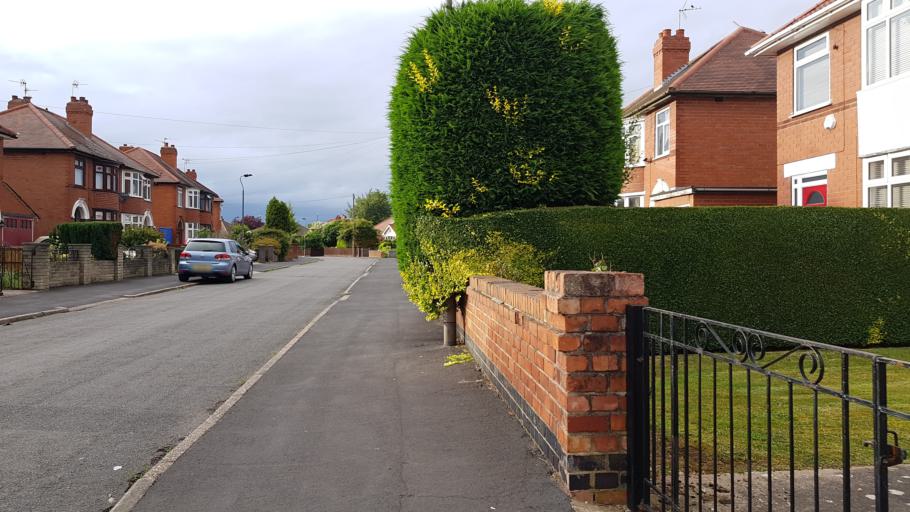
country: GB
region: England
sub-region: Derby
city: Derby
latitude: 52.8883
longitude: -1.4401
